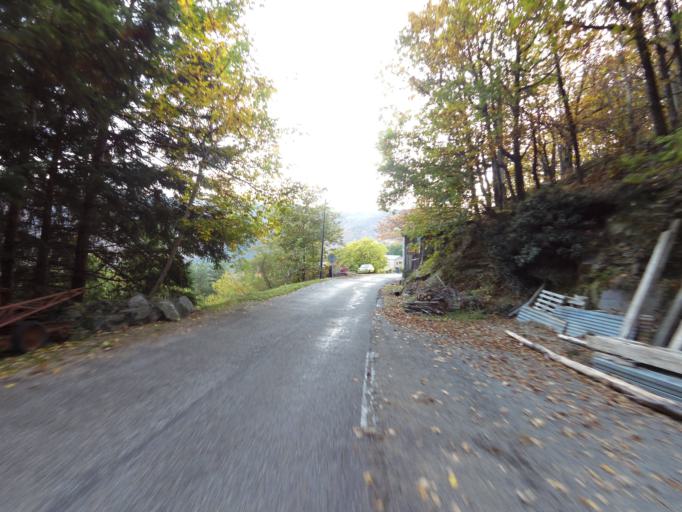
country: FR
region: Rhone-Alpes
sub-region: Departement de l'Ardeche
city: Les Vans
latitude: 44.5337
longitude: 4.0757
